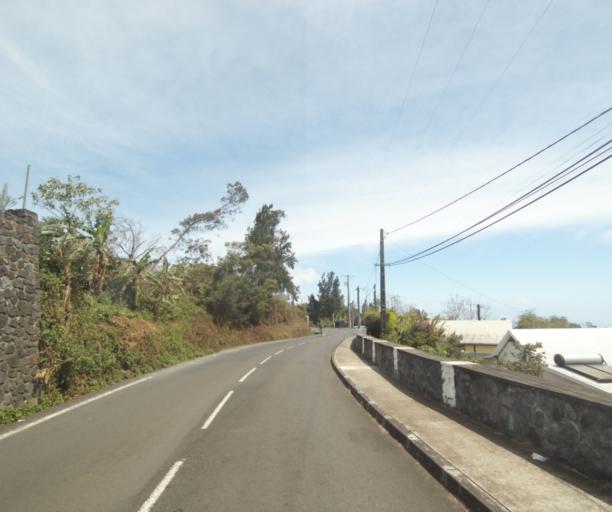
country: RE
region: Reunion
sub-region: Reunion
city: Trois-Bassins
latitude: -21.0602
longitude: 55.3081
